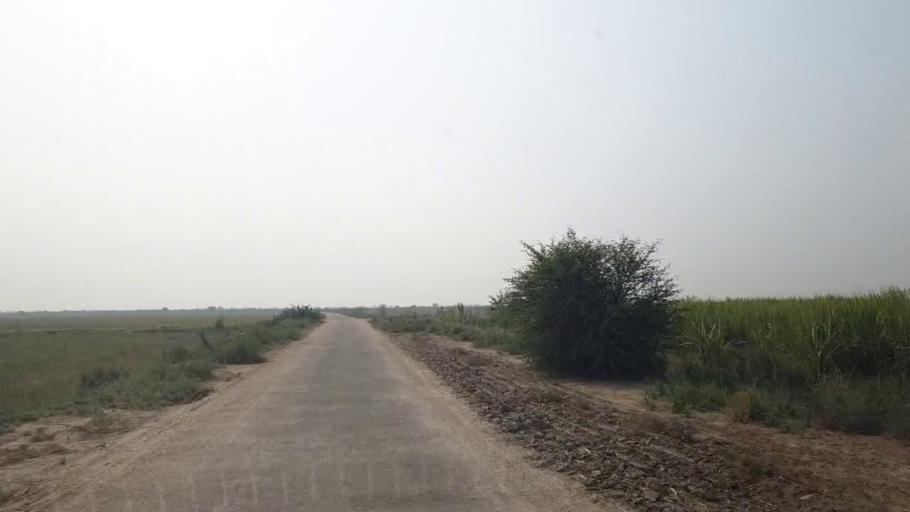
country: PK
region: Sindh
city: Matli
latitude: 25.1206
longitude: 68.6446
